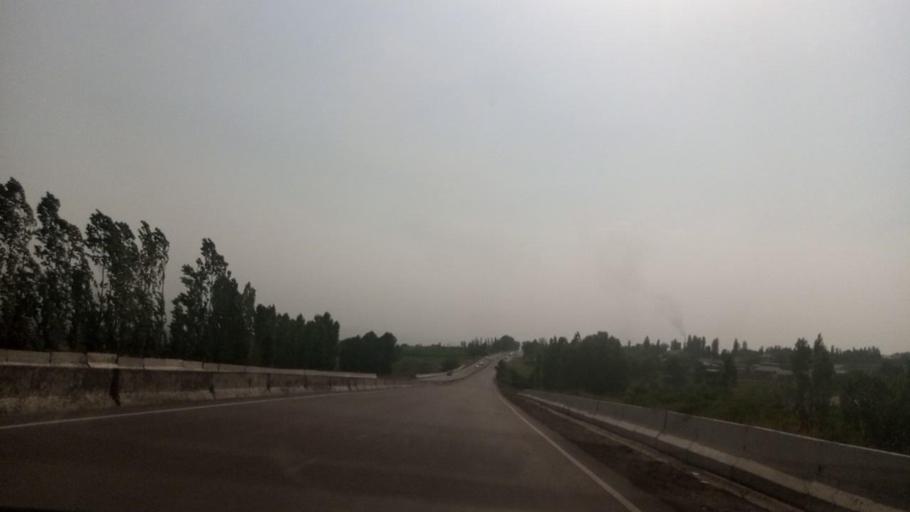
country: UZ
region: Toshkent
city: Angren
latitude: 40.9407
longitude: 69.9039
